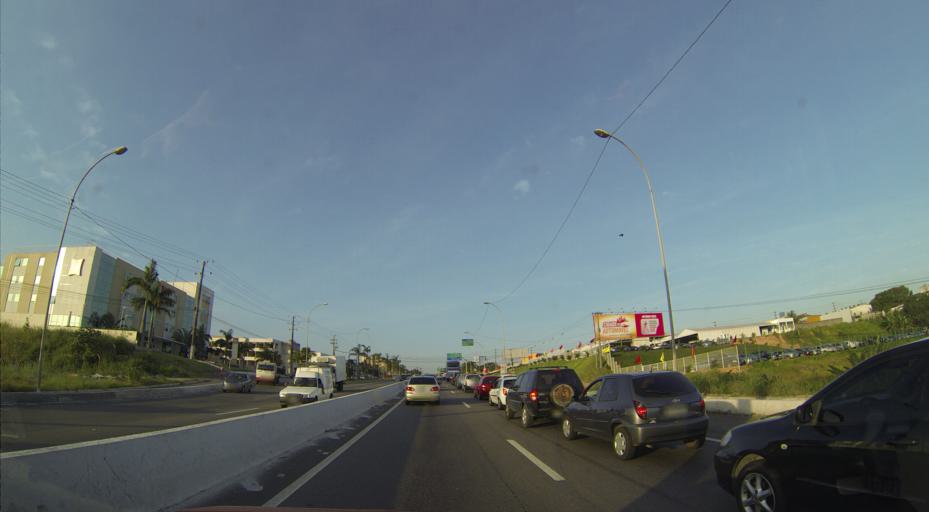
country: BR
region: Espirito Santo
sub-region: Vila Velha
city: Vila Velha
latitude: -20.2392
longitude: -40.2789
